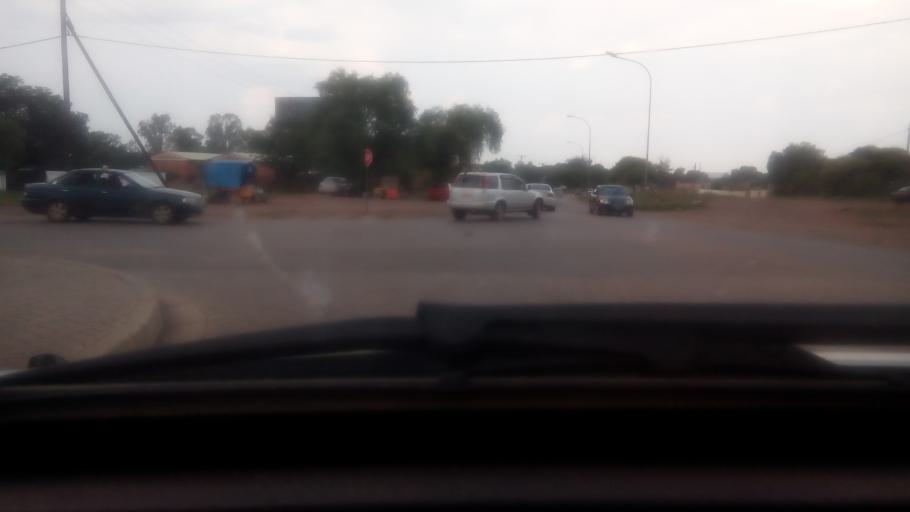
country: BW
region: Kweneng
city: Molepolole
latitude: -24.4117
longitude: 25.4883
